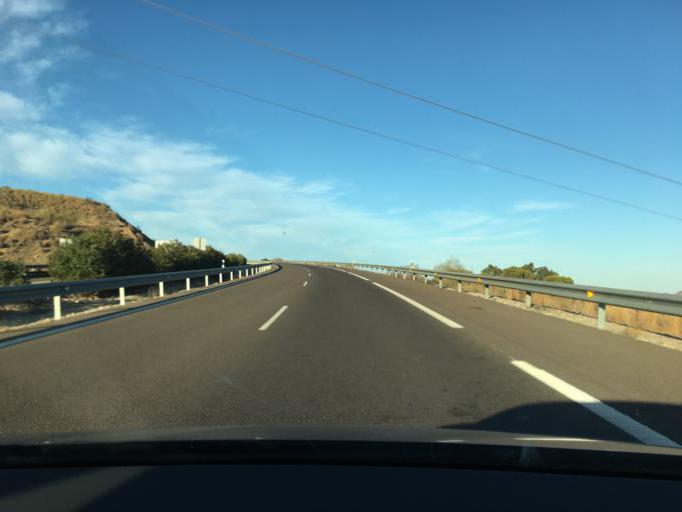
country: ES
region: Andalusia
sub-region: Provincia de Almeria
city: Bedar
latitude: 37.1376
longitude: -2.0015
